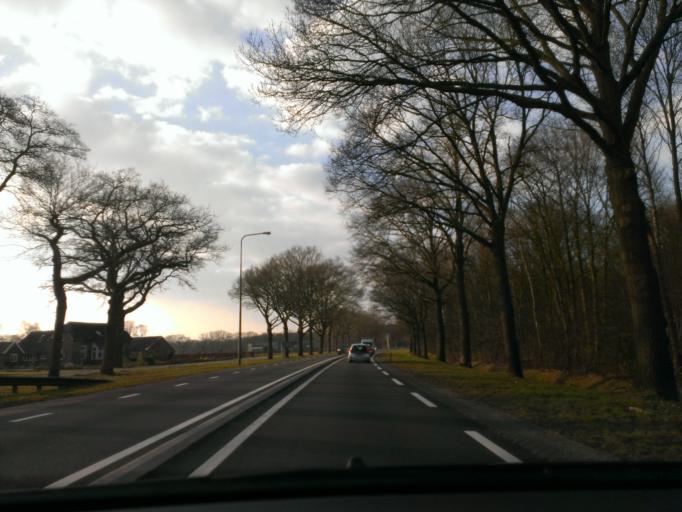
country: NL
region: Overijssel
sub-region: Gemeente Raalte
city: Raalte
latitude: 52.4038
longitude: 6.2627
